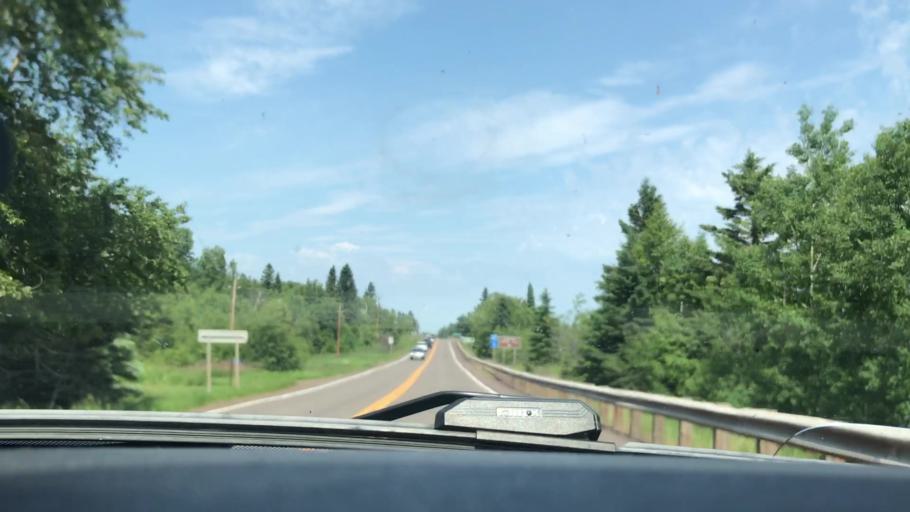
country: US
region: Minnesota
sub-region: Lake County
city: Silver Bay
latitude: 47.5746
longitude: -90.8351
